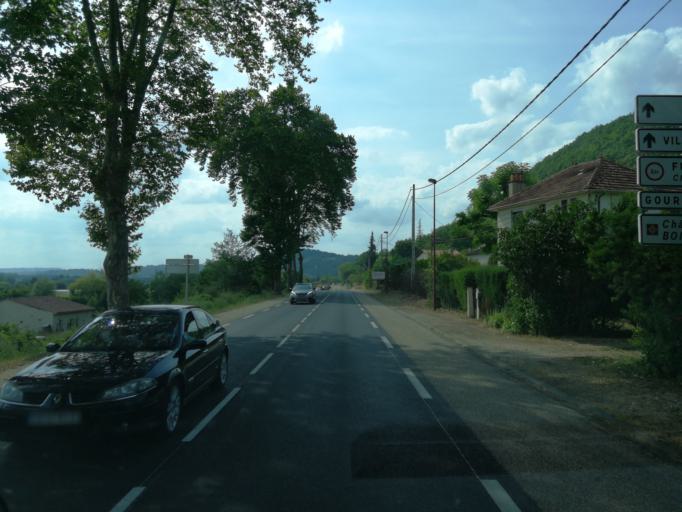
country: FR
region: Aquitaine
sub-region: Departement du Lot-et-Garonne
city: Montayral
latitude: 44.4931
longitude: 1.0001
